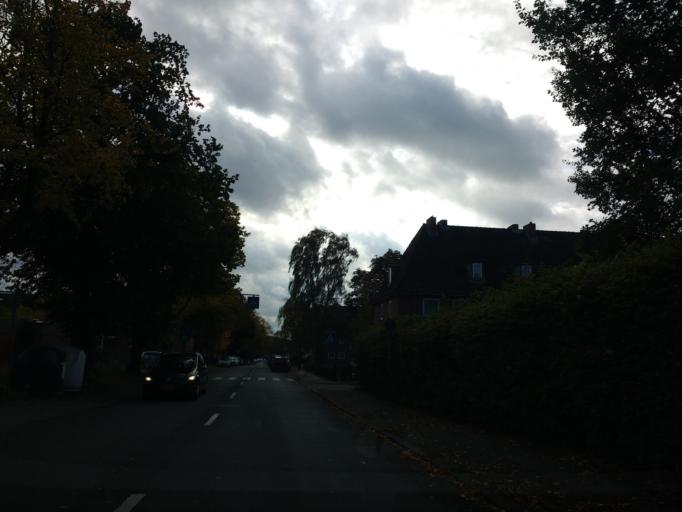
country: DE
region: Schleswig-Holstein
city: Travemuende
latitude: 53.9704
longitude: 10.8700
